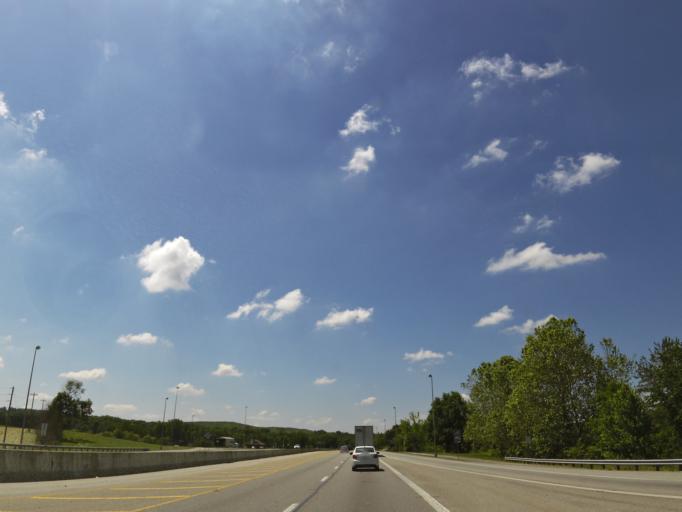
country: US
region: Kentucky
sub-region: Laurel County
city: London
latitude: 37.0457
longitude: -84.0989
